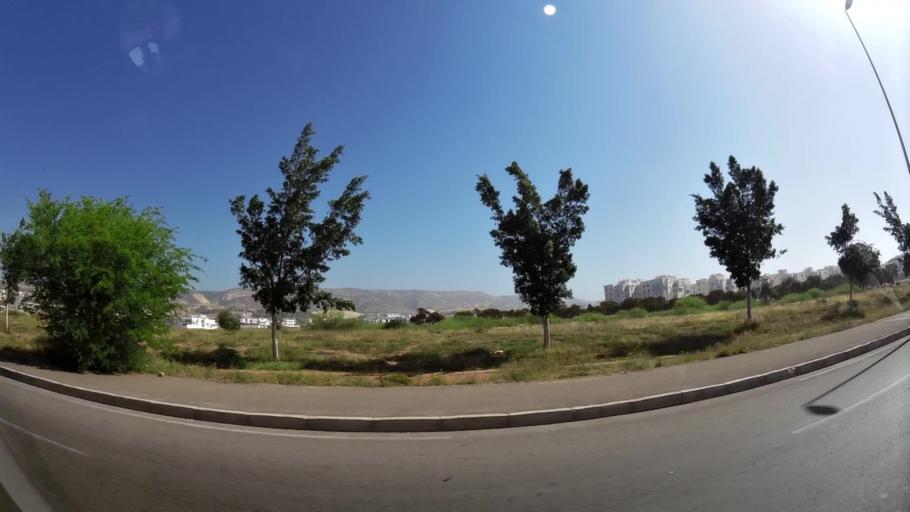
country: MA
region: Souss-Massa-Draa
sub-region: Agadir-Ida-ou-Tnan
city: Agadir
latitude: 30.4343
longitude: -9.5766
